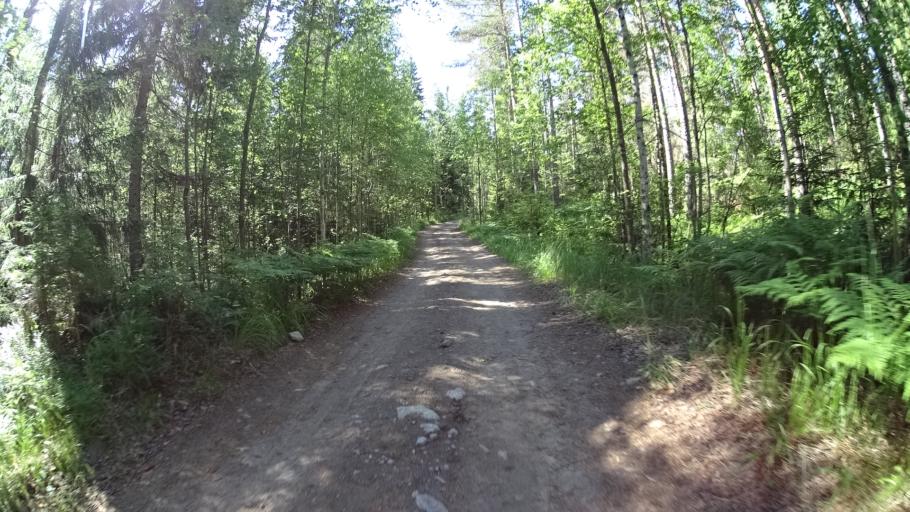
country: FI
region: Uusimaa
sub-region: Helsinki
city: Vihti
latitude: 60.3277
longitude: 24.4609
